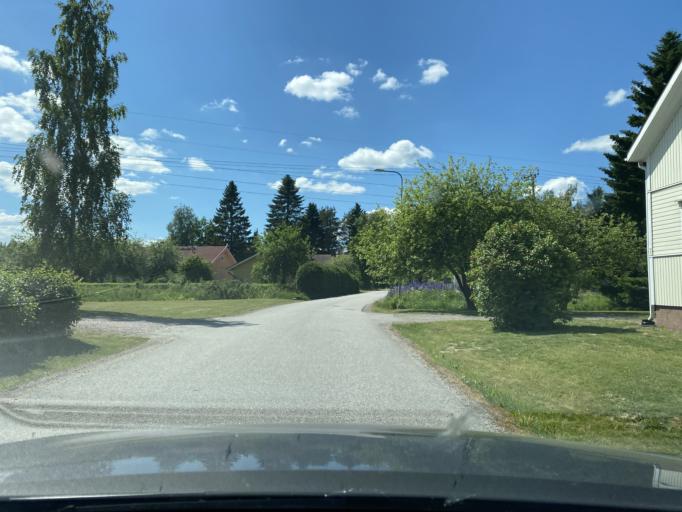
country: FI
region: Satakunta
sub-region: Rauma
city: Eura
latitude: 61.1142
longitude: 22.1427
